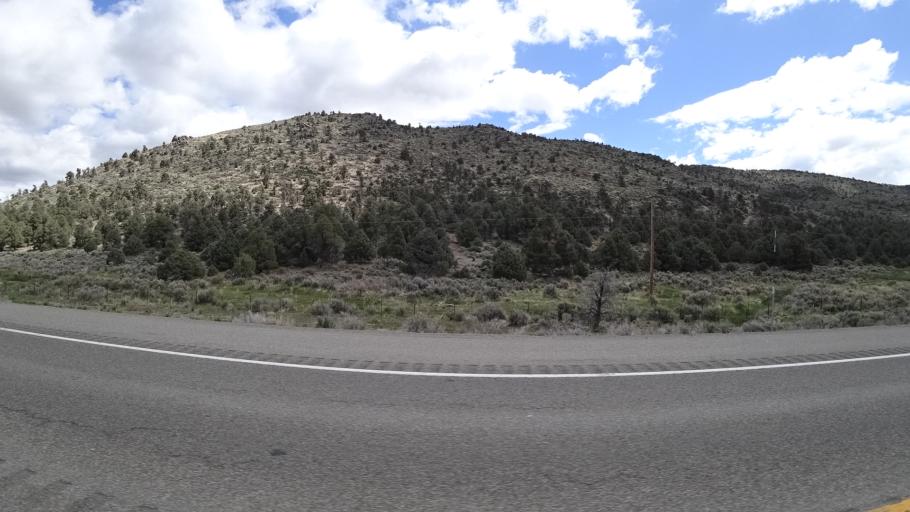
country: US
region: Nevada
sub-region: Douglas County
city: Gardnerville Ranchos
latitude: 38.7762
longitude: -119.5841
